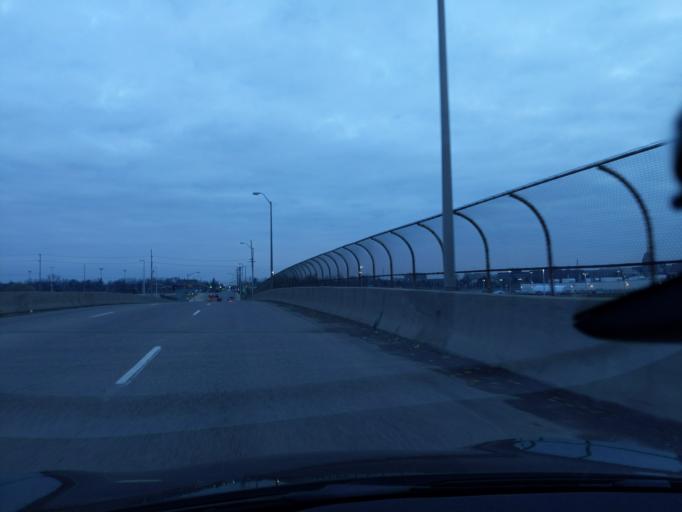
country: US
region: Michigan
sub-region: Ingham County
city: Lansing
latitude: 42.7212
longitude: -84.5673
